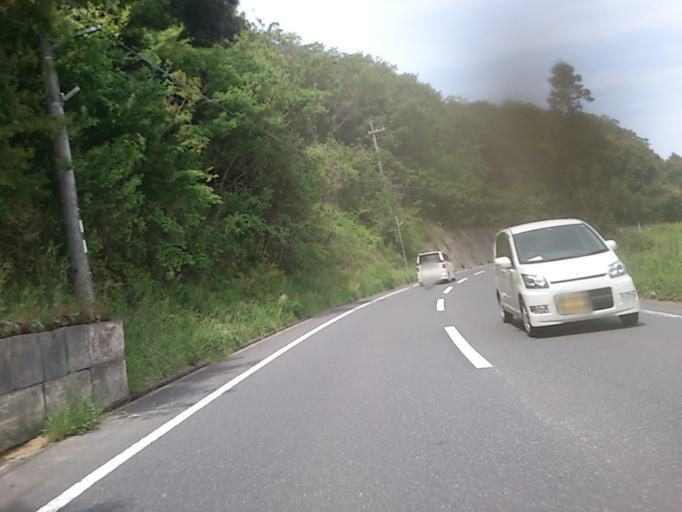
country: JP
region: Kyoto
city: Miyazu
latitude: 35.6479
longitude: 135.0848
